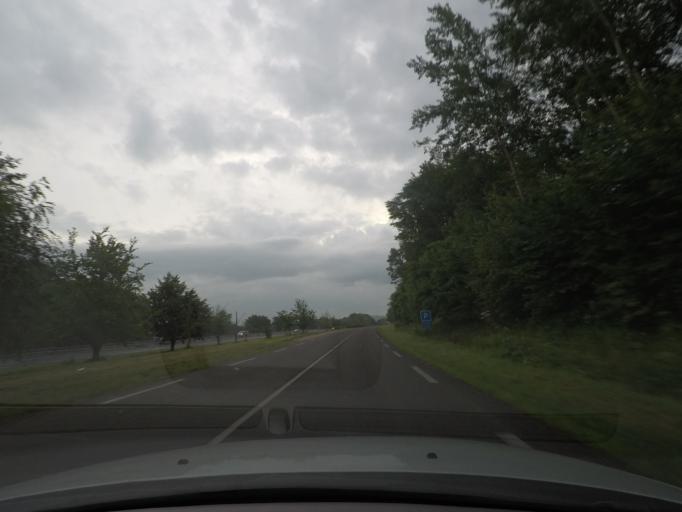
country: FR
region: Haute-Normandie
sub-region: Departement de la Seine-Maritime
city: Neufchatel-en-Bray
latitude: 49.7181
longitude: 1.4201
